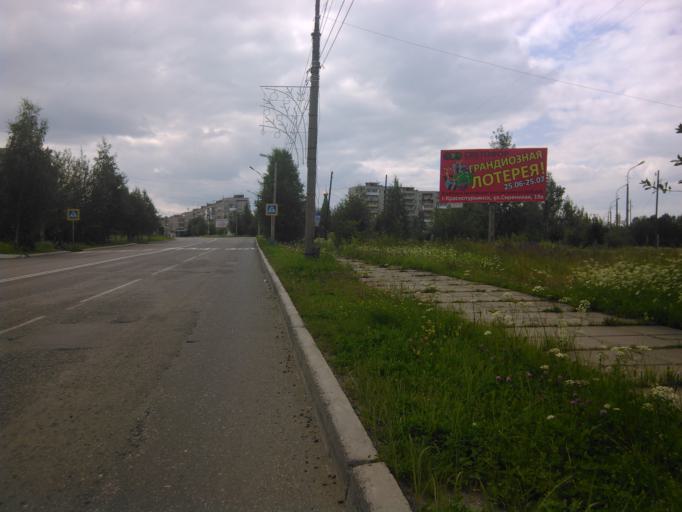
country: RU
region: Sverdlovsk
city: Krasnotur'insk
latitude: 59.7594
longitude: 60.1711
